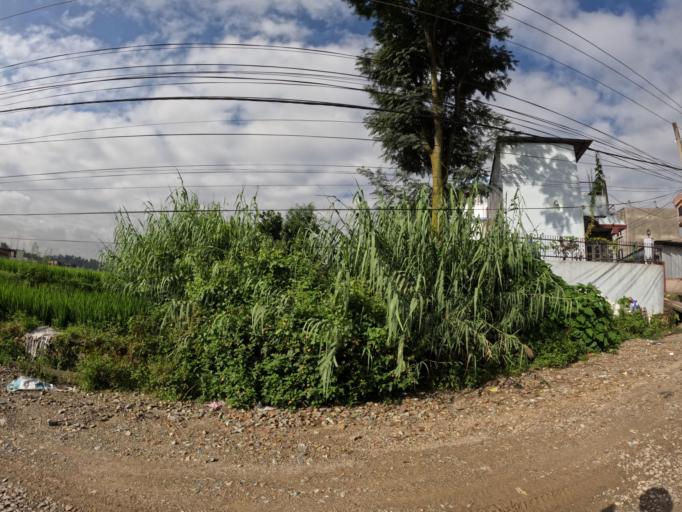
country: NP
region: Central Region
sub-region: Bagmati Zone
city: Kathmandu
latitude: 27.7660
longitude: 85.3347
